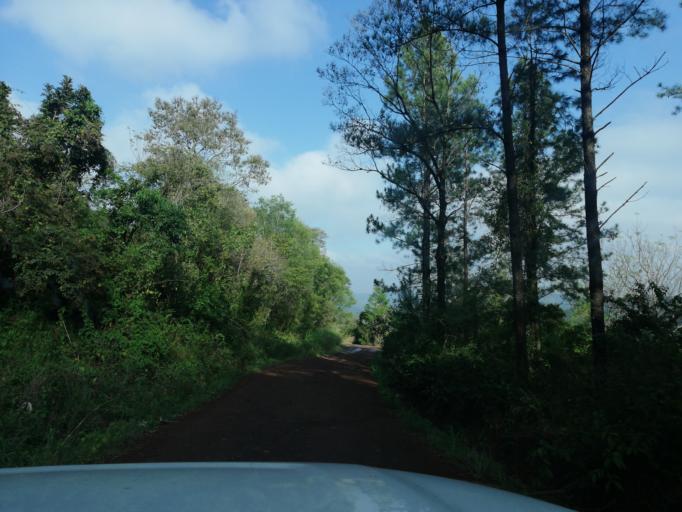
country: AR
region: Misiones
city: Cerro Azul
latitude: -27.5800
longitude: -55.5136
